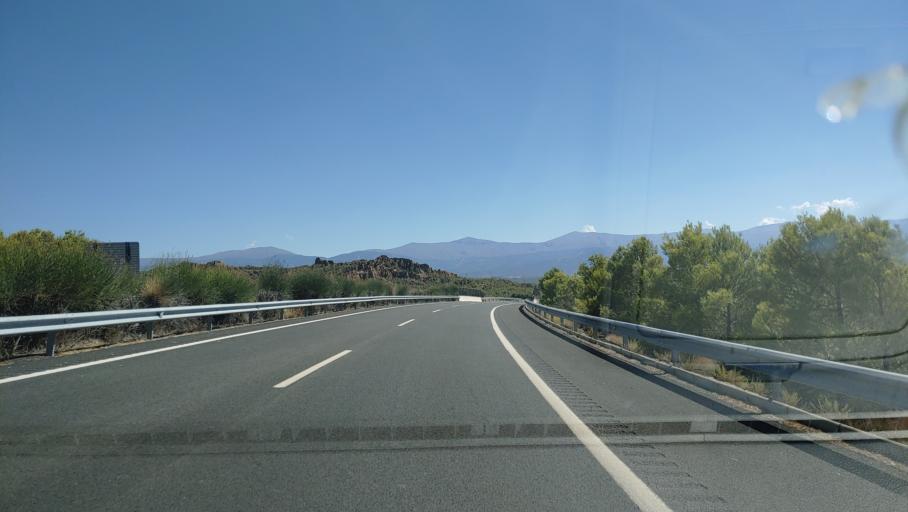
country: ES
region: Andalusia
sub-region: Provincia de Granada
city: Guadix
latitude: 37.3001
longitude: -3.1100
